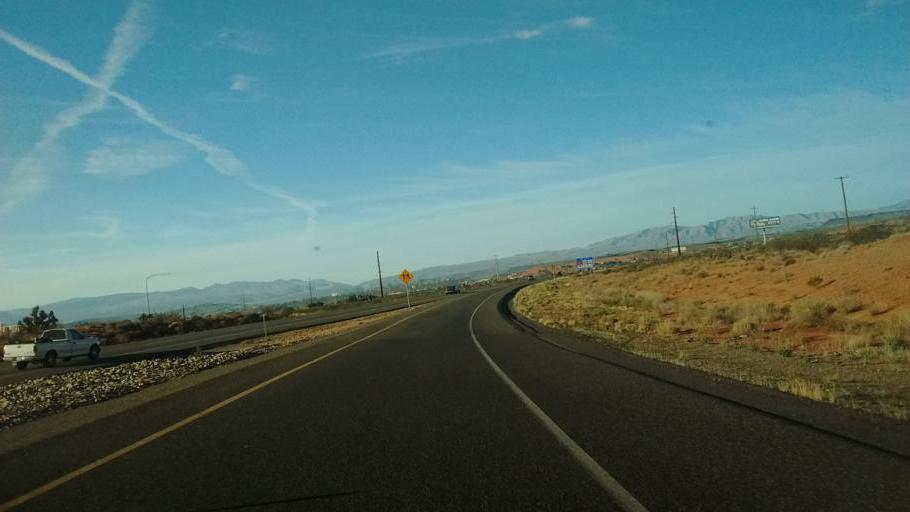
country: US
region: Utah
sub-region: Washington County
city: Washington
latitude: 37.1463
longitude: -113.4910
